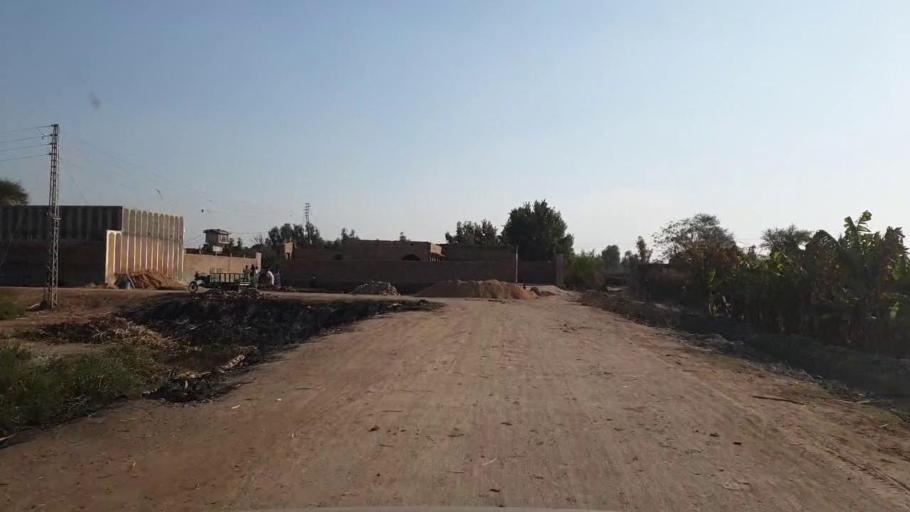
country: PK
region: Sindh
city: Tando Allahyar
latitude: 25.3572
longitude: 68.7034
